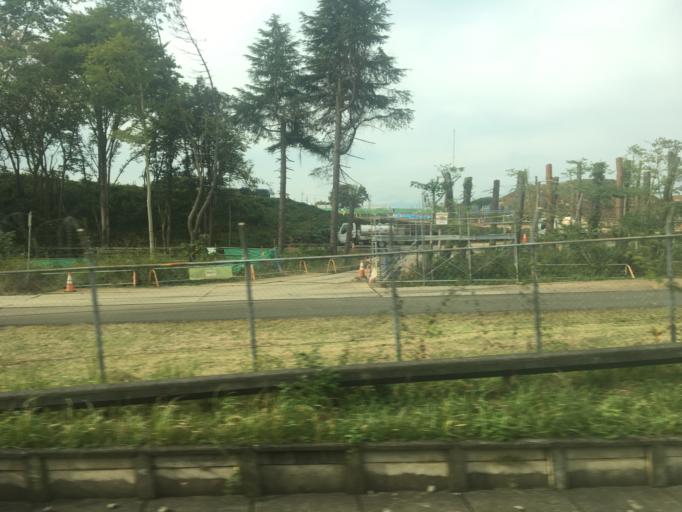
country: JP
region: Saitama
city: Sayama
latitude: 35.8428
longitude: 139.4198
